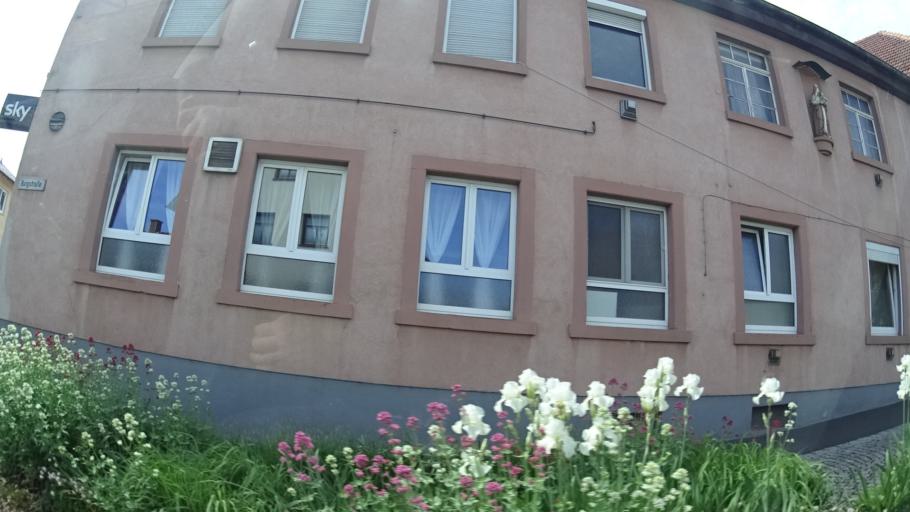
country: DE
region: Bavaria
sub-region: Regierungsbezirk Unterfranken
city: Birkenfeld
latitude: 49.8587
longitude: 9.6951
